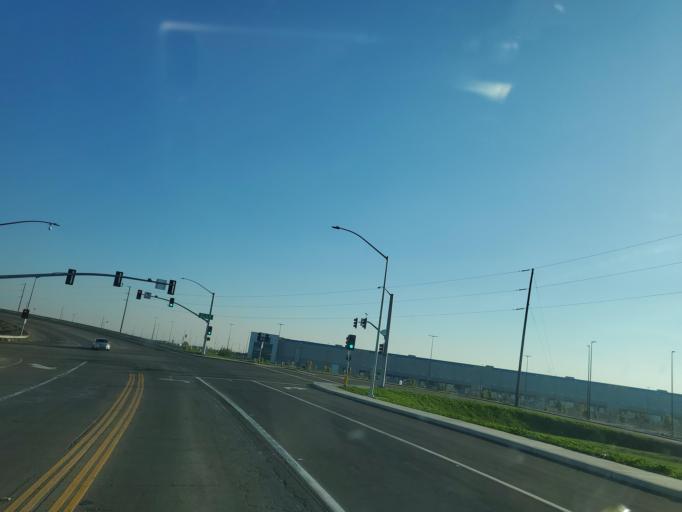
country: US
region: California
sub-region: San Joaquin County
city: Garden Acres
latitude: 37.9135
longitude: -121.1874
